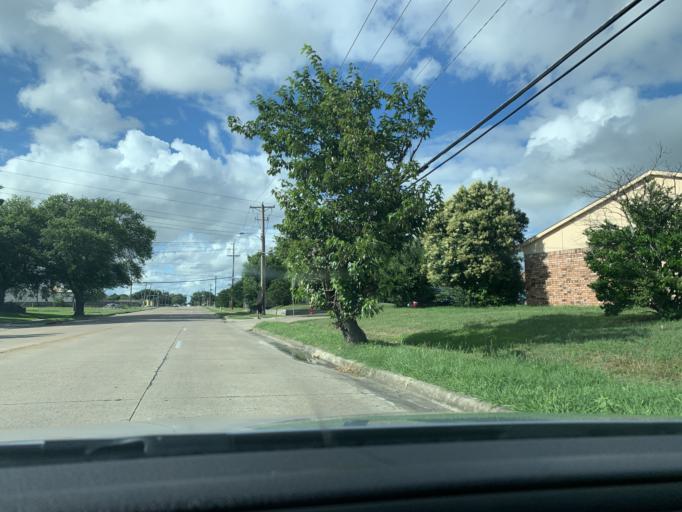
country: US
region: Texas
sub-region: Dallas County
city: Grand Prairie
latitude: 32.6558
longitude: -97.0277
